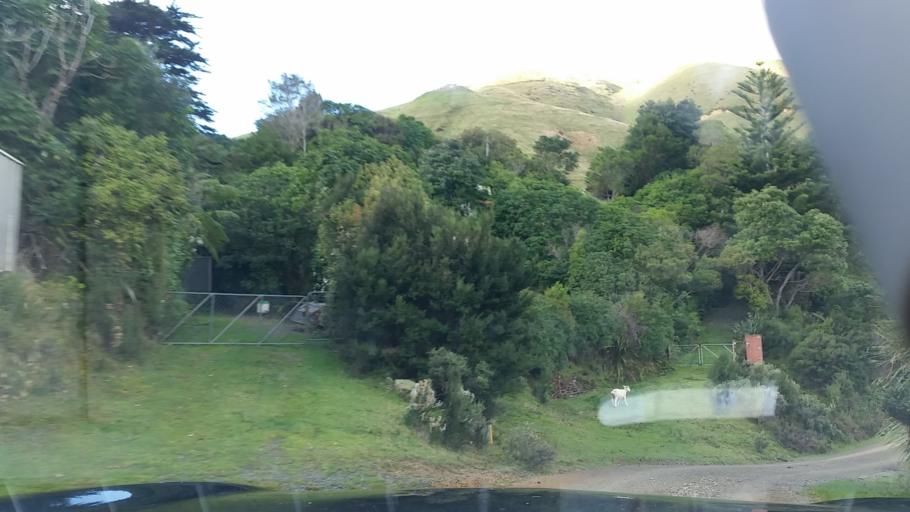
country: NZ
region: Marlborough
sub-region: Marlborough District
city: Picton
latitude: -40.9885
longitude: 173.8275
